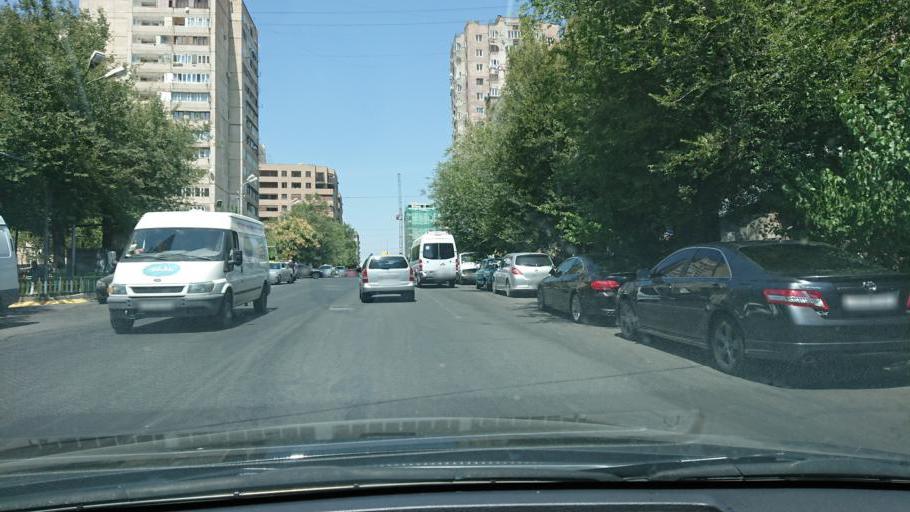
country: AM
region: Yerevan
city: Yerevan
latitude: 40.1974
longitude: 44.5025
